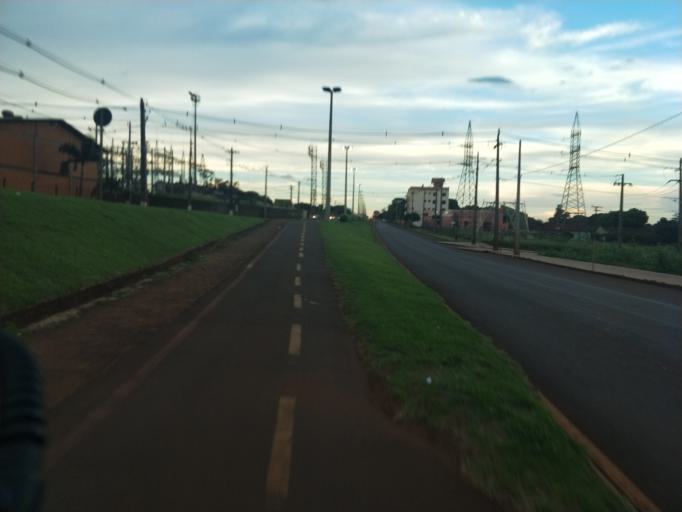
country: BR
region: Parana
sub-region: Marechal Candido Rondon
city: Marechal Candido Rondon
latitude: -24.5566
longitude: -54.0478
